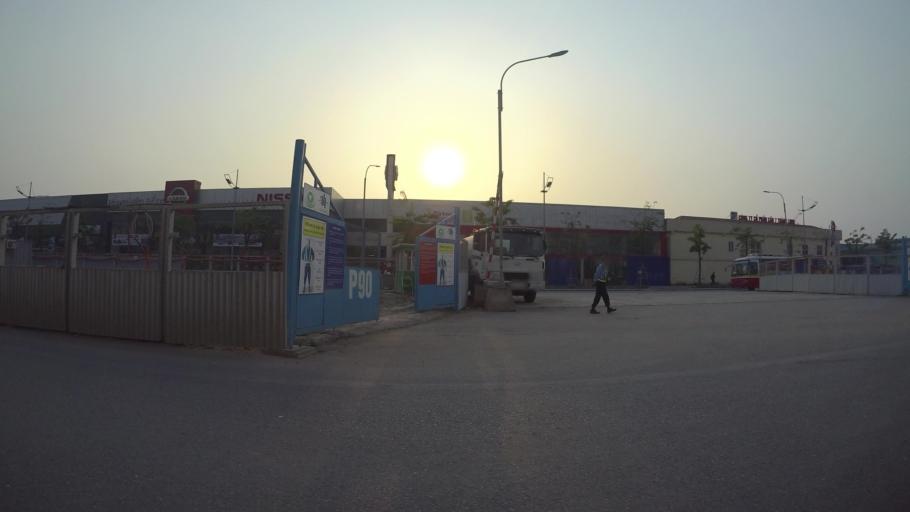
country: VN
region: Ha Noi
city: Tay Ho
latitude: 21.0730
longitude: 105.7857
